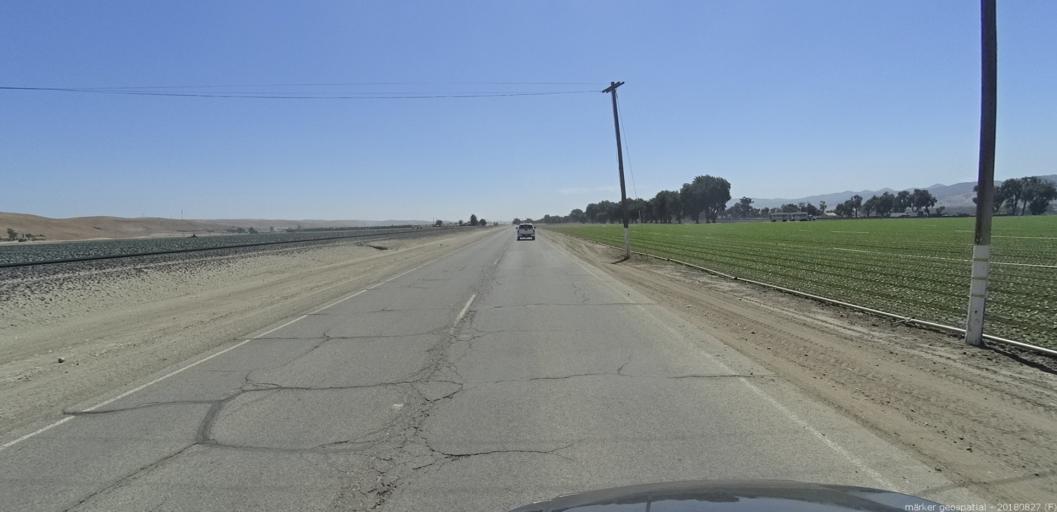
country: US
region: California
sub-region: Monterey County
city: King City
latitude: 36.0319
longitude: -120.9086
